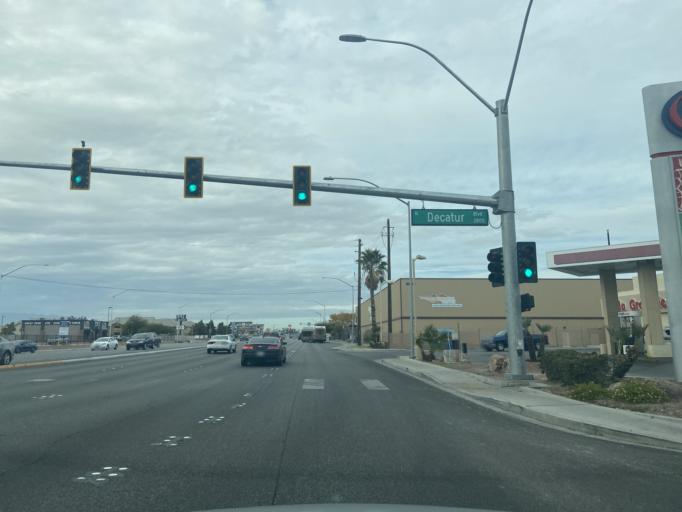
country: US
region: Nevada
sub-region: Clark County
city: Las Vegas
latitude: 36.2098
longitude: -115.2052
